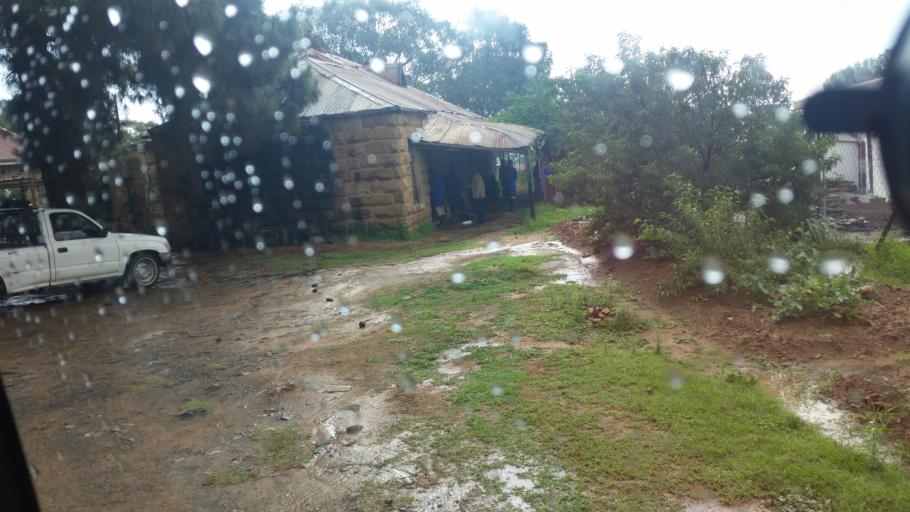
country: LS
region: Mohale's Hoek District
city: Mohale's Hoek
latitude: -30.1526
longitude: 27.4750
